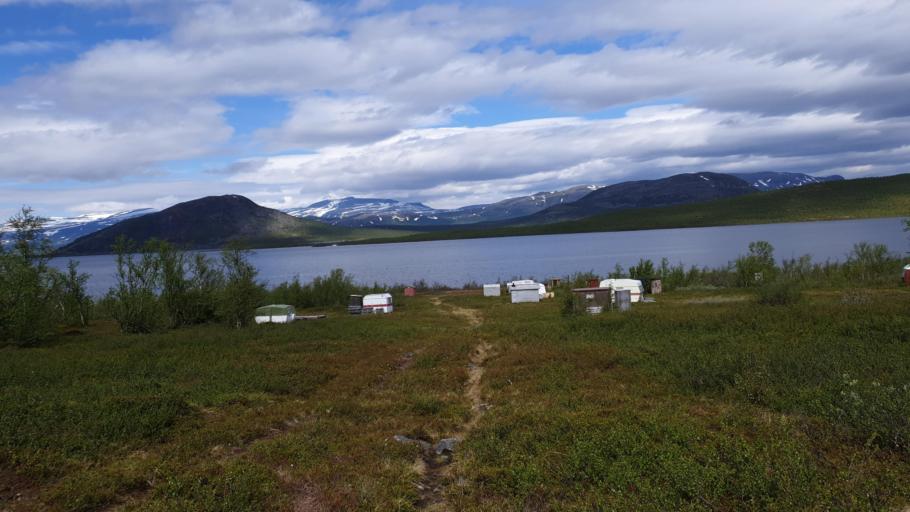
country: SE
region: Norrbotten
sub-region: Kiruna Kommun
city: Kiruna
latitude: 68.2335
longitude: 19.6192
